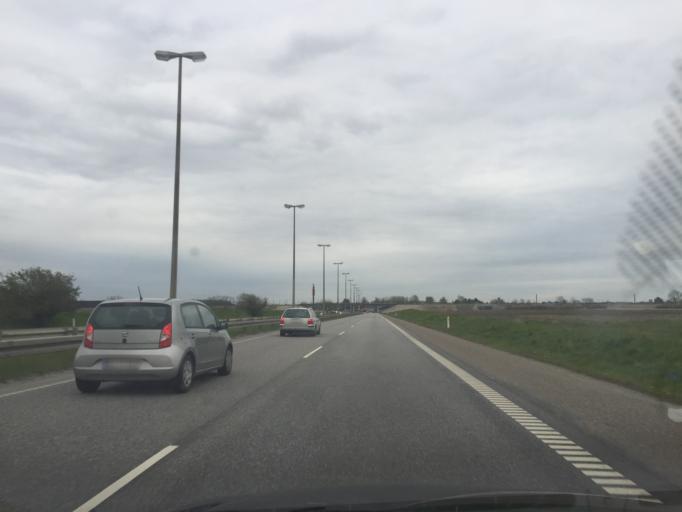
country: DK
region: Capital Region
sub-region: Hoje-Taastrup Kommune
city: Taastrup
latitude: 55.6252
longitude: 12.3137
